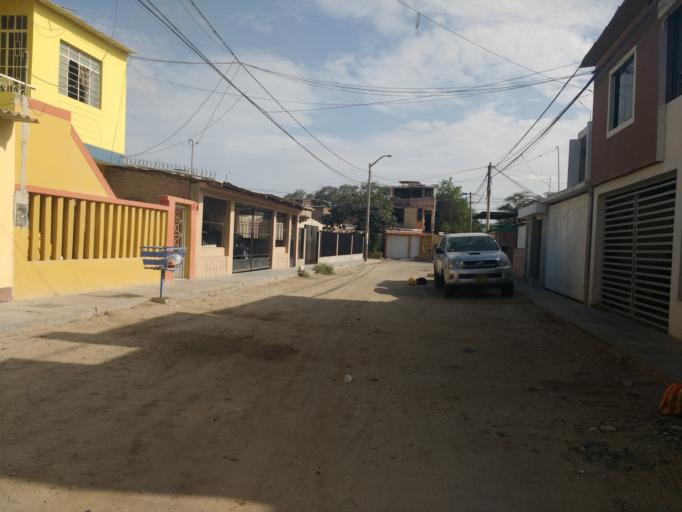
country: PE
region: Piura
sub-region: Provincia de Piura
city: Piura
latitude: -5.1921
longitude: -80.6453
